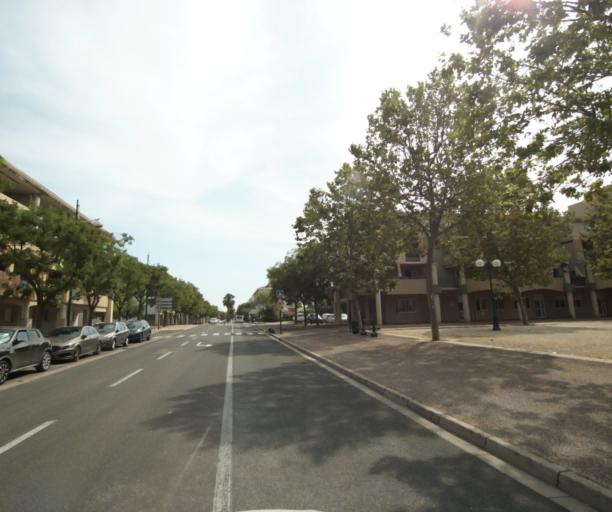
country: FR
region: Provence-Alpes-Cote d'Azur
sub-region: Departement du Var
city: La Garde
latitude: 43.1325
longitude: 6.0197
